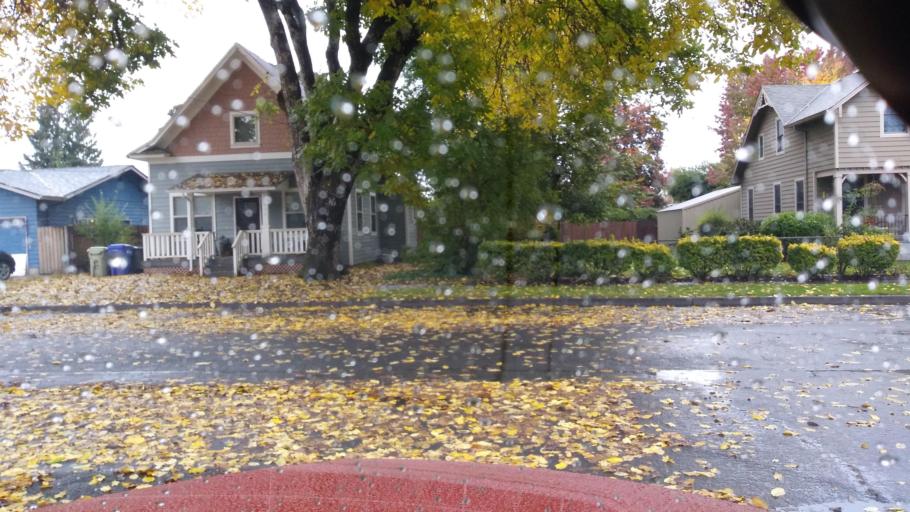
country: US
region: Oregon
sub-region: Washington County
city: Cornelius
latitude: 45.5183
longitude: -123.0536
